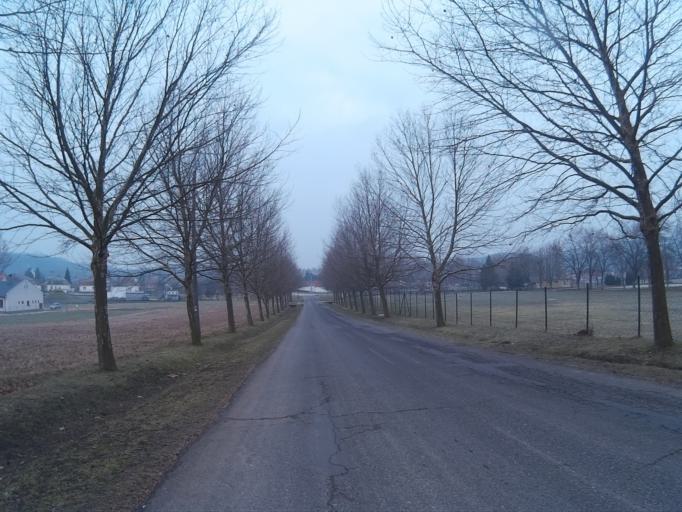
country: HU
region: Komarom-Esztergom
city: Tarjan
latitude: 47.6091
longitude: 18.5104
